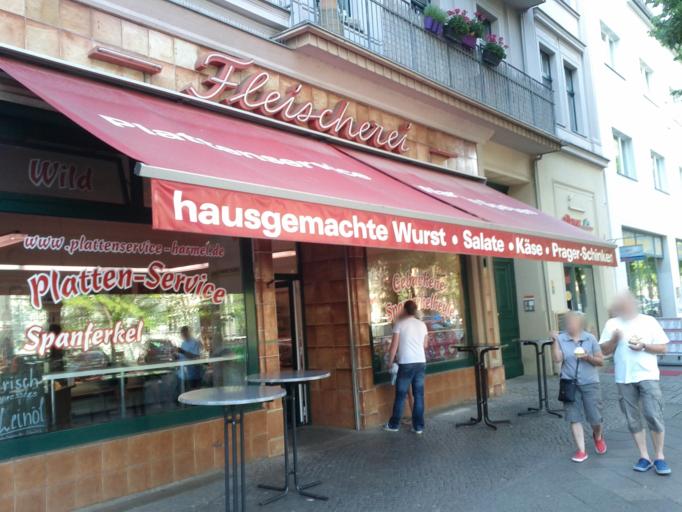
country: DE
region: Berlin
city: Friedrichshagen
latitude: 52.4528
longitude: 13.6249
